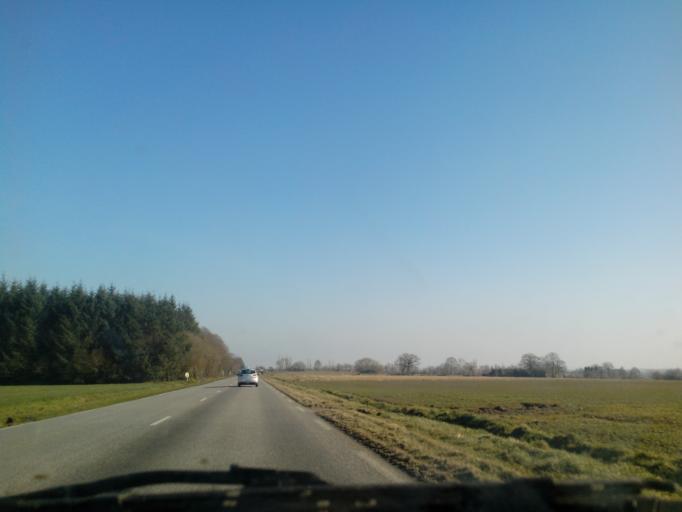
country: FR
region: Brittany
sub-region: Departement des Cotes-d'Armor
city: Merdrignac
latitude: 48.1971
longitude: -2.4687
